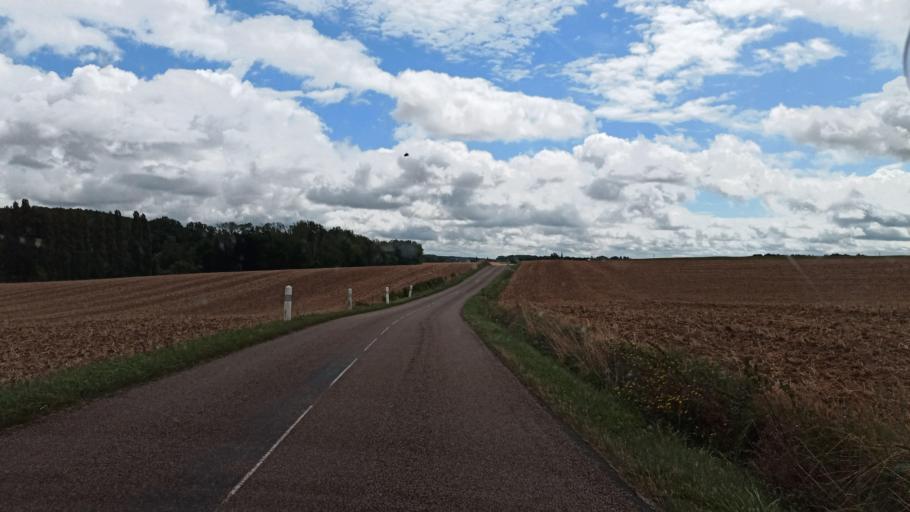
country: FR
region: Bourgogne
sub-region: Departement de l'Yonne
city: Saint-Valerien
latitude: 48.2271
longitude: 3.0637
